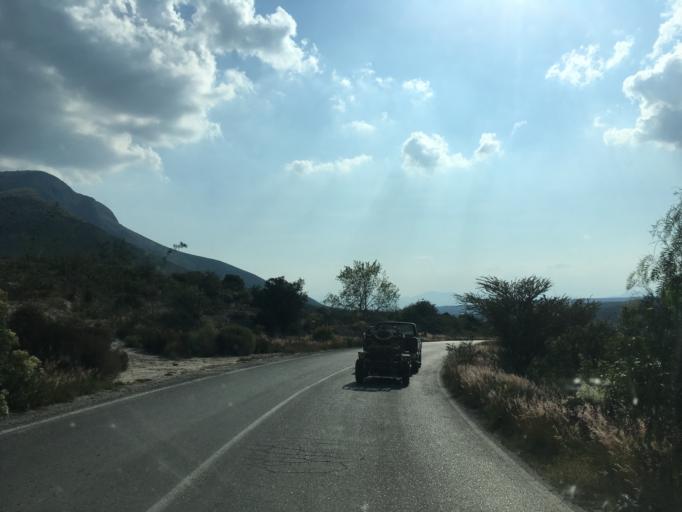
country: MX
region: Hidalgo
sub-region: Cardonal
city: Pozuelos
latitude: 20.6061
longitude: -99.1060
